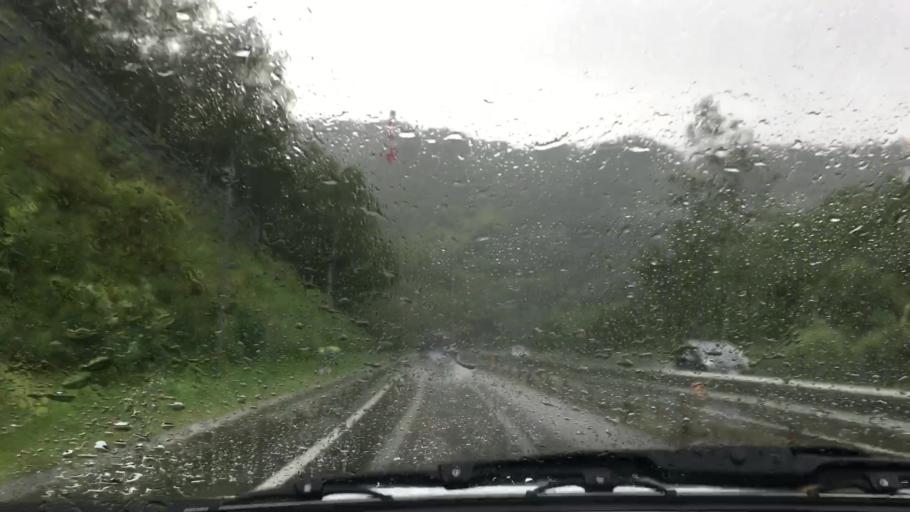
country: JP
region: Hokkaido
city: Otaru
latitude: 42.8488
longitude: 141.0397
